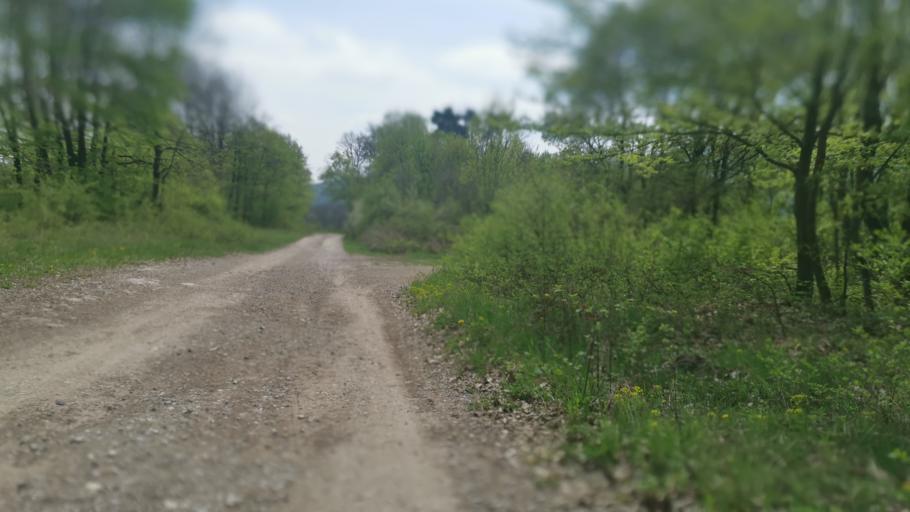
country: SK
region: Trnavsky
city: Smolenice
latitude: 48.5483
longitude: 17.4416
